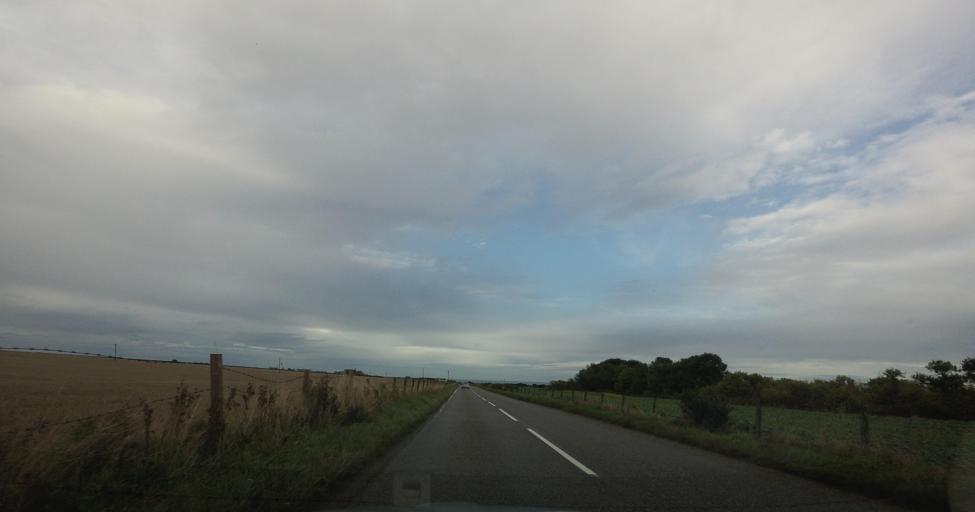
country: GB
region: Scotland
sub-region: Moray
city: Portknockie
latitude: 57.6933
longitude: -2.8592
